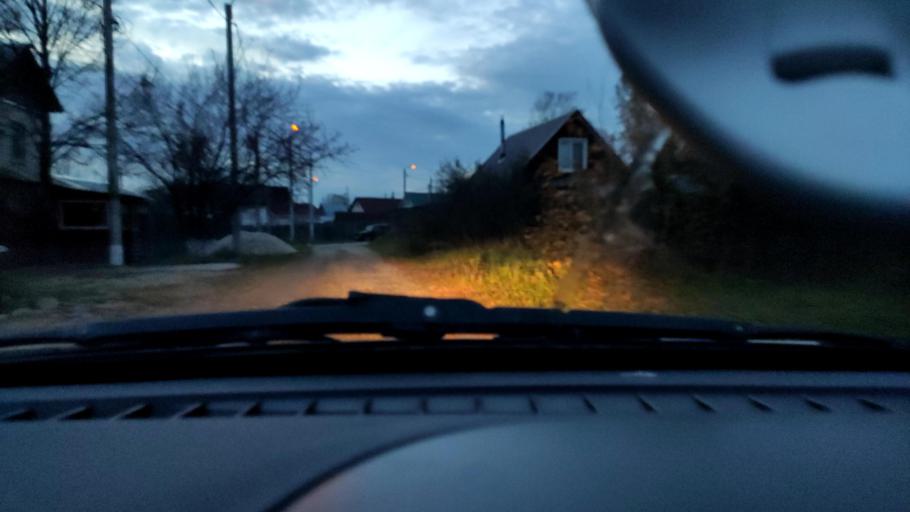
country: RU
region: Perm
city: Perm
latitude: 57.9752
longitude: 56.2955
